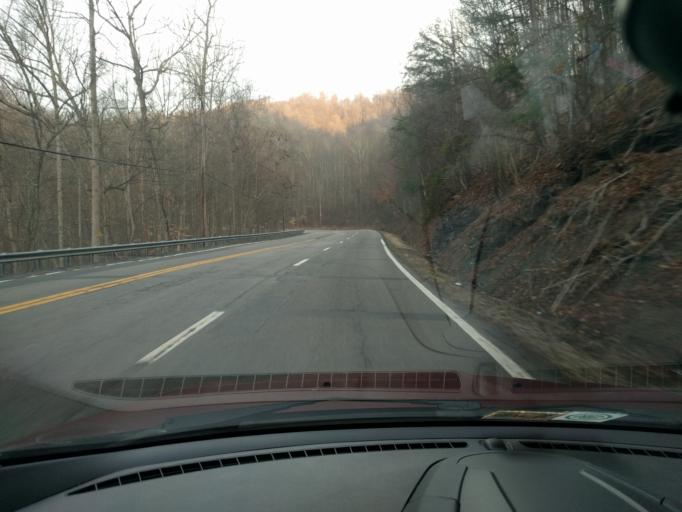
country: US
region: West Virginia
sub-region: Fayette County
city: Ansted
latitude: 38.1415
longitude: -81.1503
